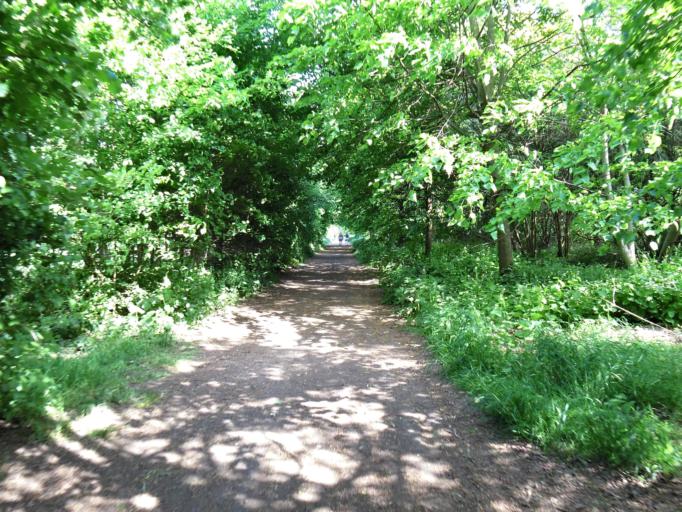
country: BE
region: Flanders
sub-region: Provincie Vlaams-Brabant
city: Wezembeek-Oppem
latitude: 50.8557
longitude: 4.5044
